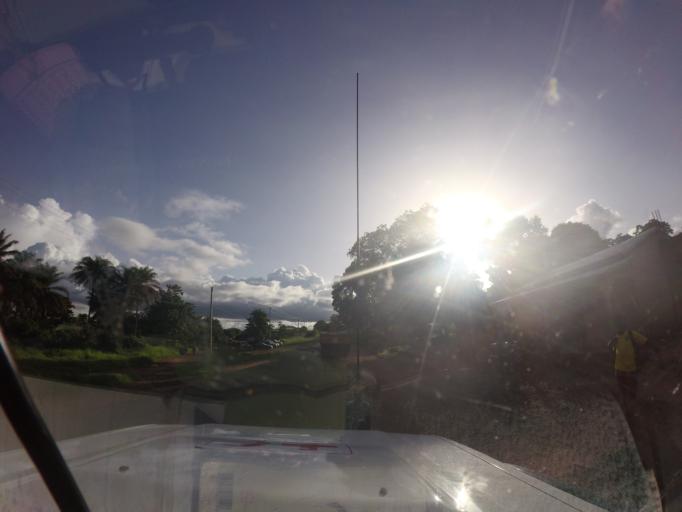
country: GN
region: Kindia
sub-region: Kindia
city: Kindia
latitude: 10.0326
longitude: -12.8630
